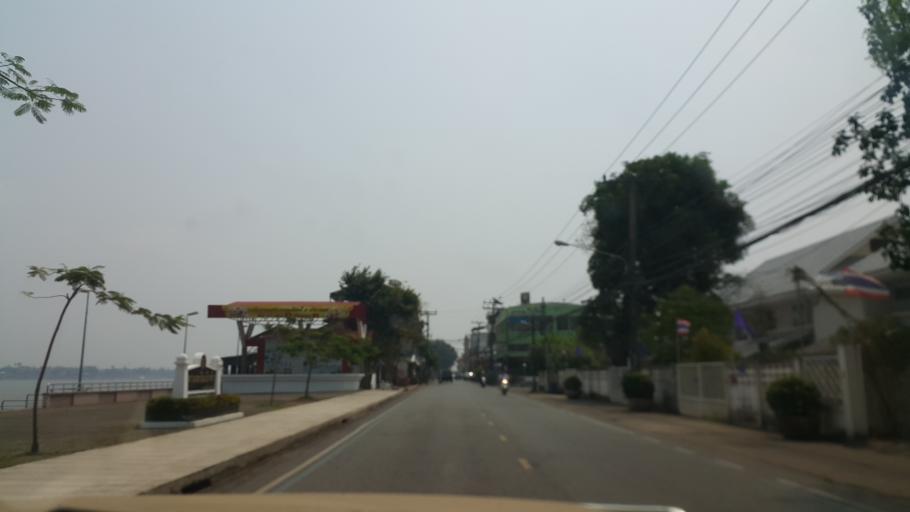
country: TH
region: Nakhon Phanom
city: Nakhon Phanom
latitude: 17.4062
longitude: 104.7865
